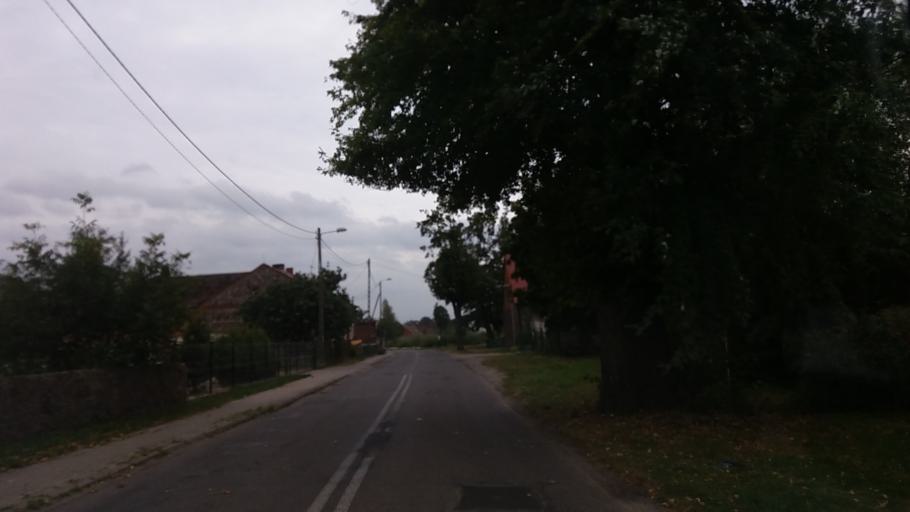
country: PL
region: Lubusz
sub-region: Powiat strzelecko-drezdenecki
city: Strzelce Krajenskie
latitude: 52.9303
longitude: 15.5616
